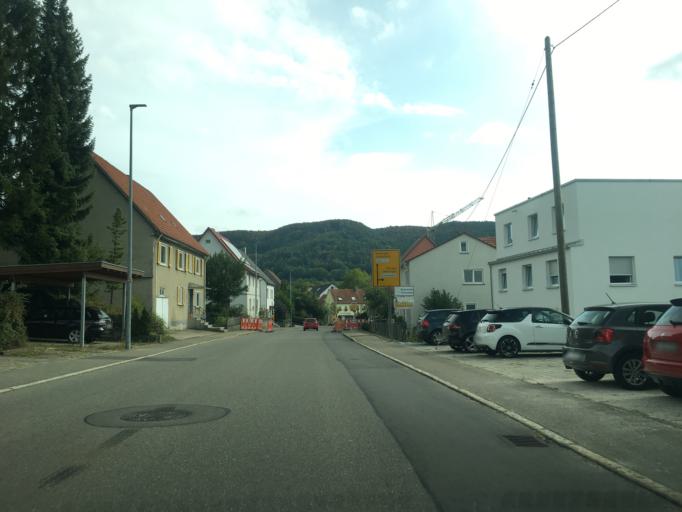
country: DE
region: Baden-Wuerttemberg
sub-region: Tuebingen Region
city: Gomaringen
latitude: 48.4367
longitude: 9.1484
